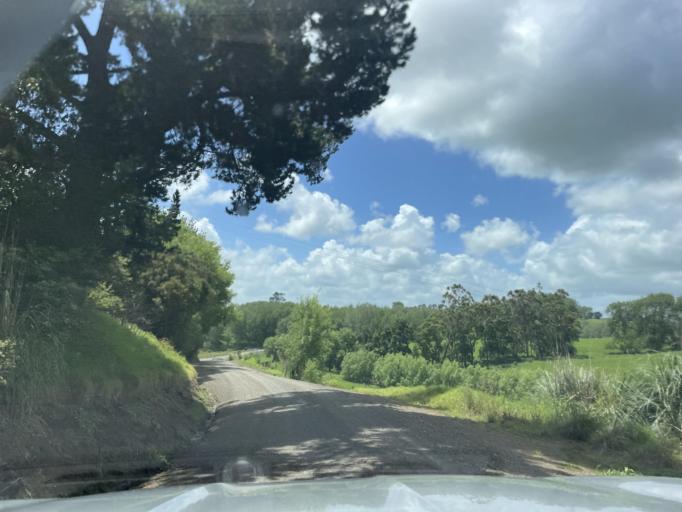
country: NZ
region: Auckland
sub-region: Auckland
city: Wellsford
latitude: -36.1792
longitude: 174.3154
